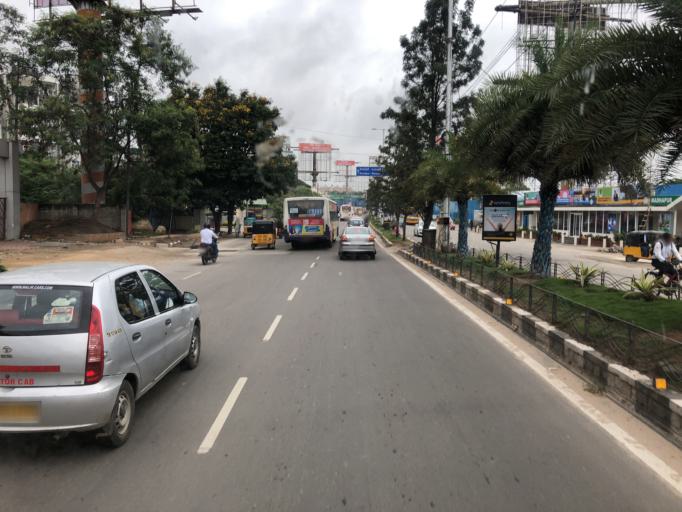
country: IN
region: Telangana
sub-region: Rangareddi
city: Kukatpalli
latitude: 17.4546
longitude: 78.3783
